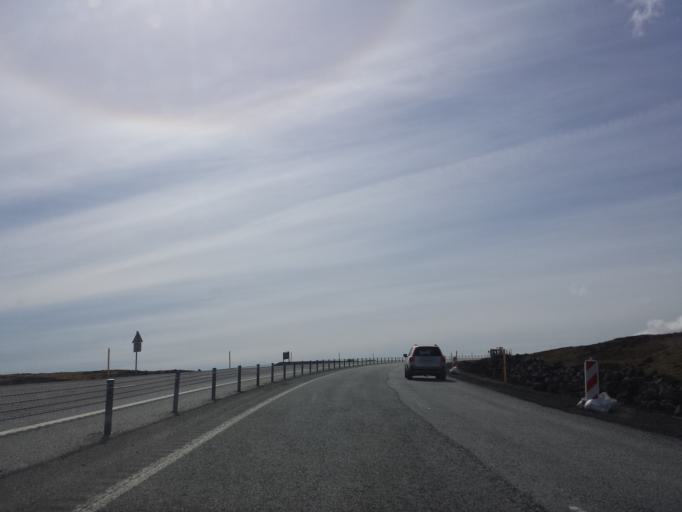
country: IS
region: South
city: Hveragerdi
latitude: 64.0137
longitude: -21.2337
